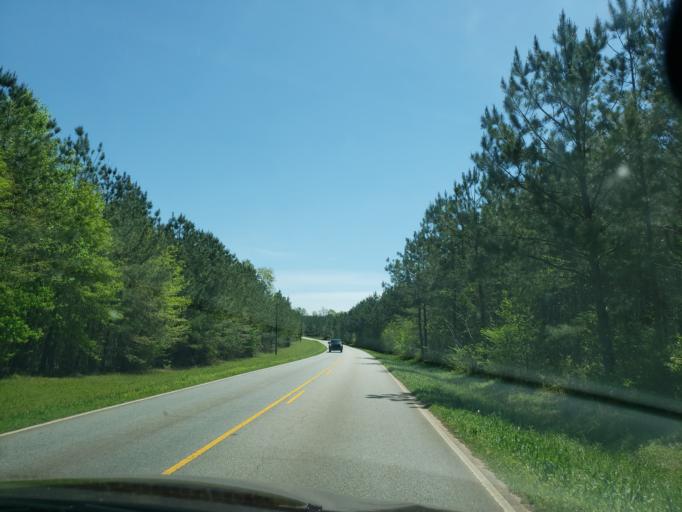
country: US
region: Alabama
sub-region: Tallapoosa County
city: Camp Hill
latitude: 32.7026
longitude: -85.7051
